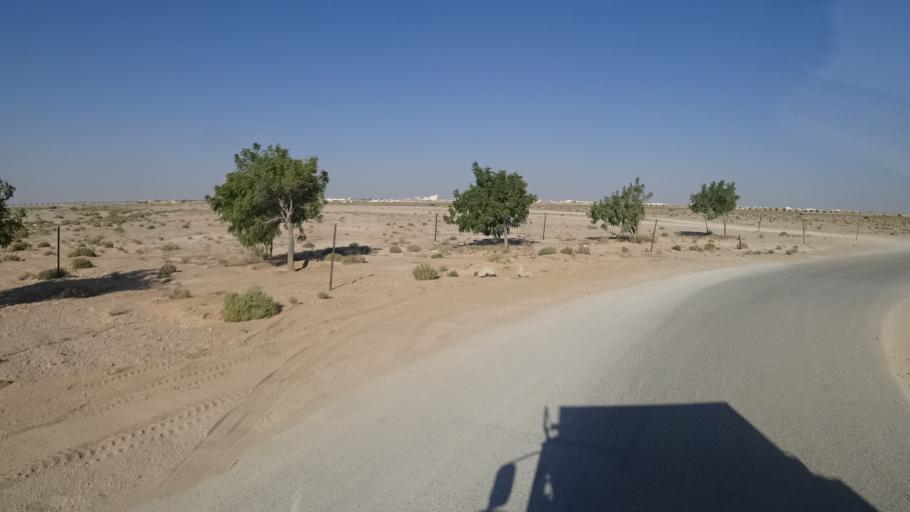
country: OM
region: Zufar
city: Salalah
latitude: 17.5959
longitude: 54.0269
